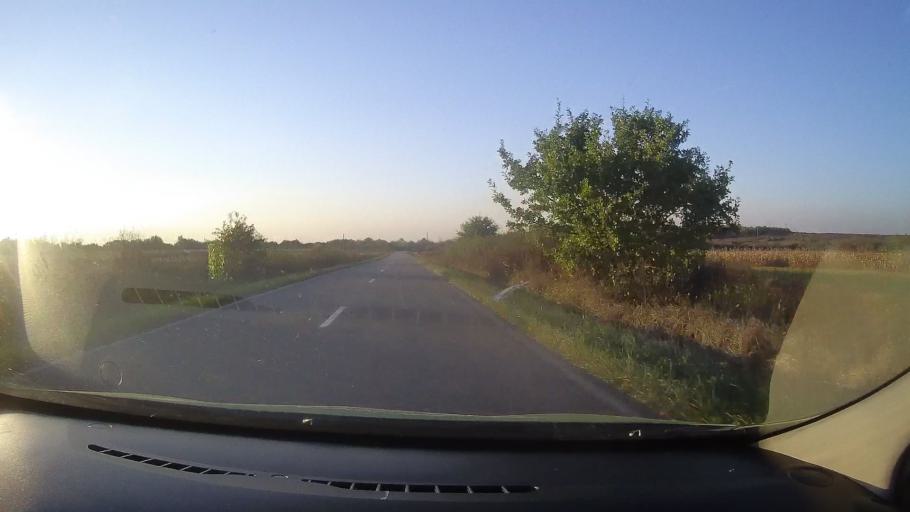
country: RO
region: Timis
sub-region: Comuna Traian Vuia
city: Traian Vuia
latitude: 45.7896
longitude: 22.0759
